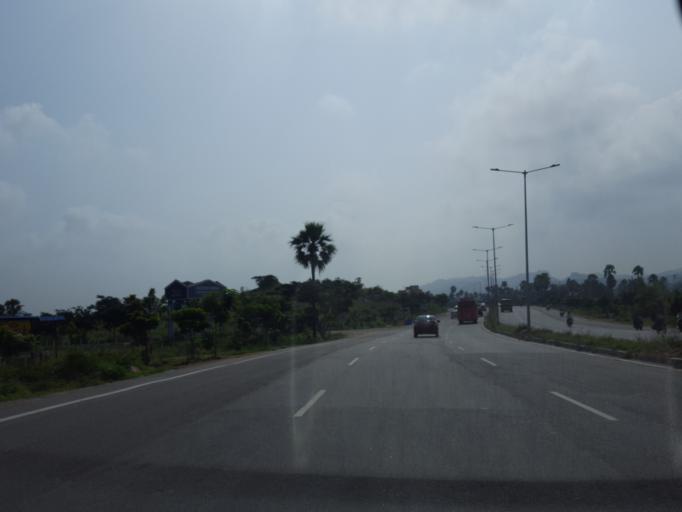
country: IN
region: Telangana
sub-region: Rangareddi
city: Ghatkesar
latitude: 17.3087
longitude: 78.7005
